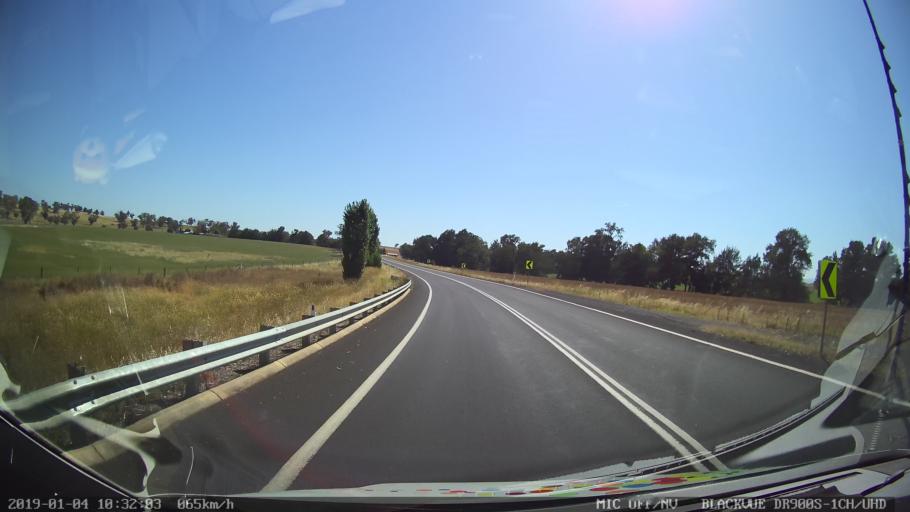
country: AU
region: New South Wales
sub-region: Cabonne
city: Canowindra
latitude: -33.3296
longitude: 148.6357
